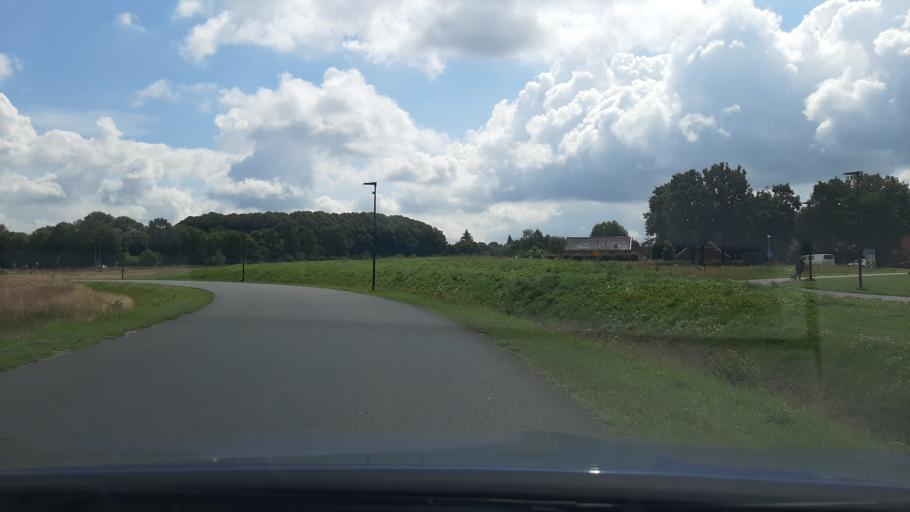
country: NL
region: Groningen
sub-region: Gemeente  Oldambt
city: Winschoten
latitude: 53.1813
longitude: 6.9640
